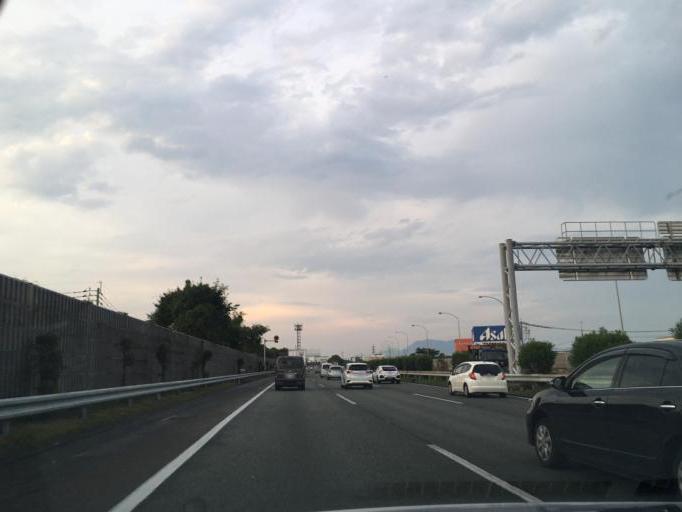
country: JP
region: Saga Prefecture
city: Tosu
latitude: 33.4052
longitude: 130.5379
